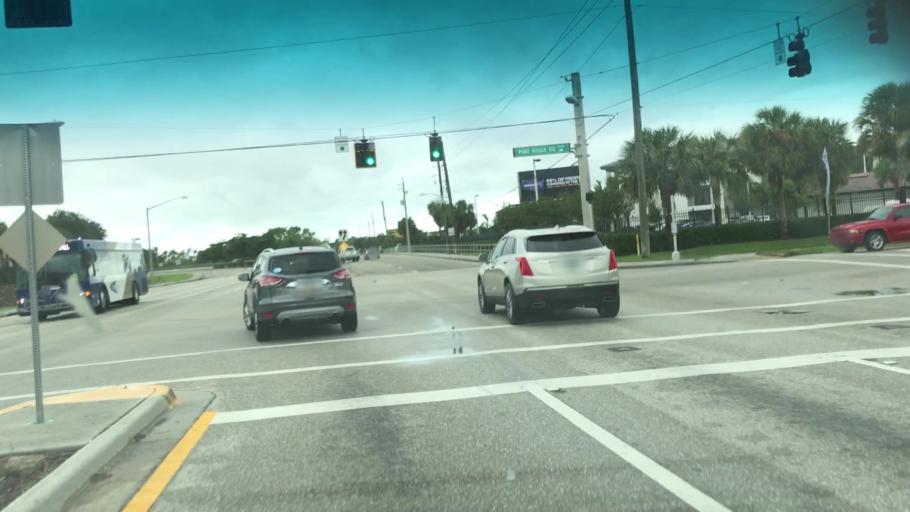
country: US
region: Florida
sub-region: Lee County
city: Harlem Heights
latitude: 26.5182
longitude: -81.9356
